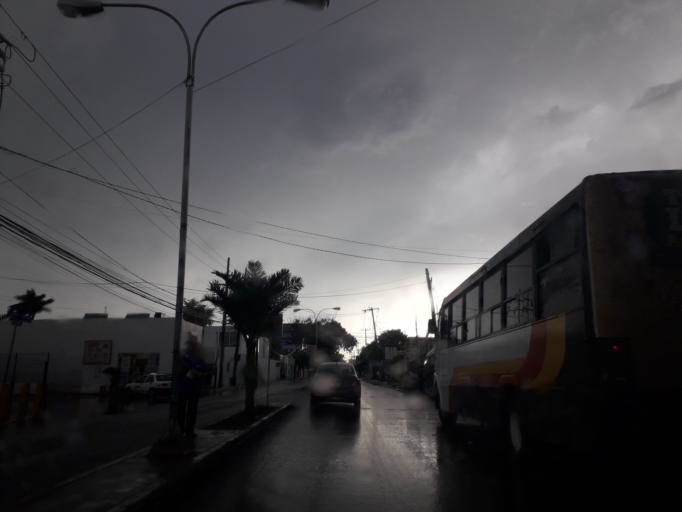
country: MX
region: Yucatan
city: Merida
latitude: 20.9756
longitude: -89.6408
